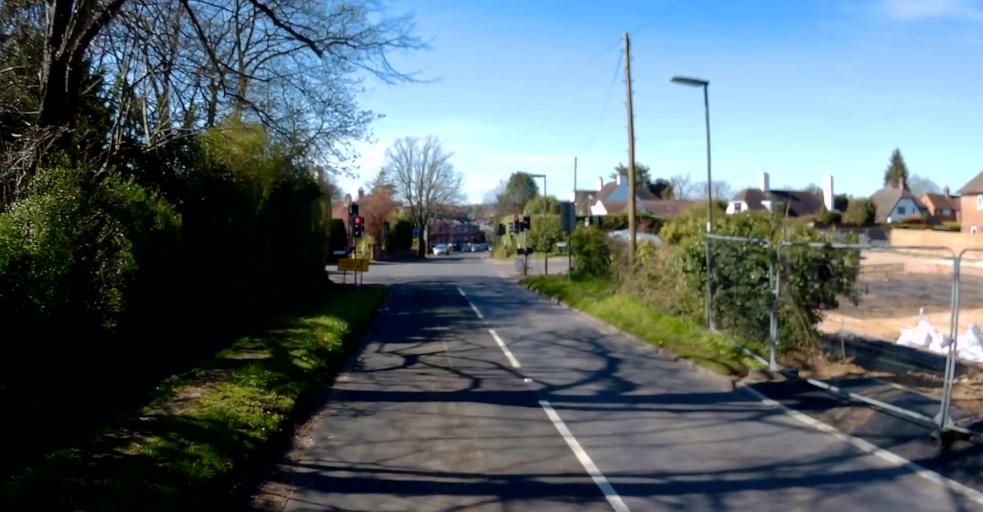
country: GB
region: England
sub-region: Surrey
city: Farnham
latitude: 51.2080
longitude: -0.7871
